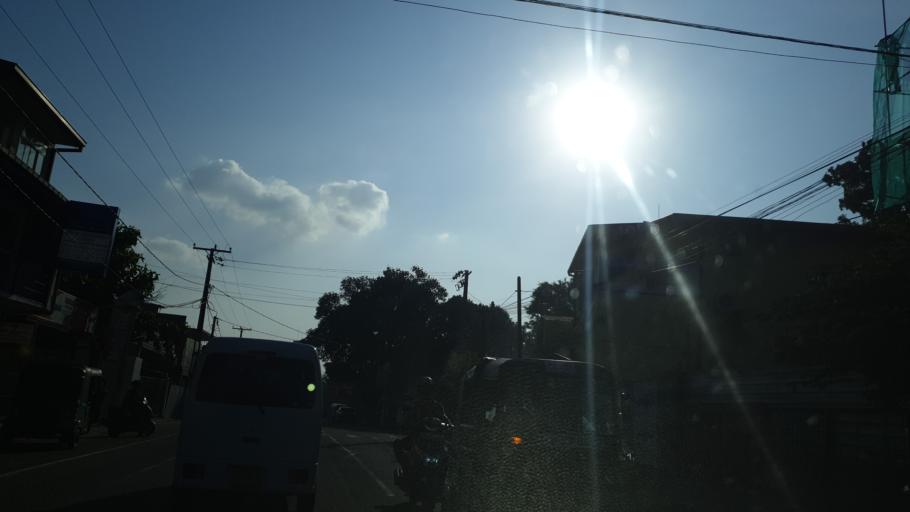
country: LK
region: Western
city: Sri Jayewardenepura Kotte
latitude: 6.8557
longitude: 79.8877
